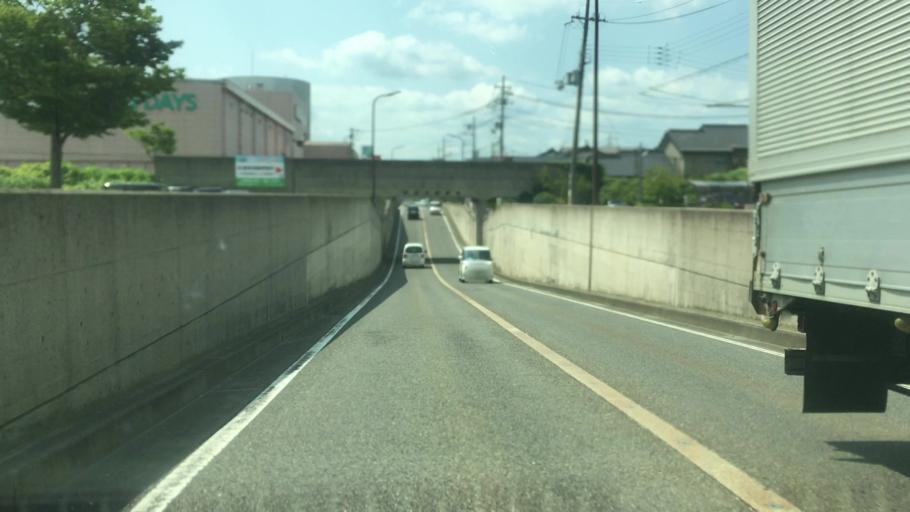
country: JP
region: Hyogo
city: Toyooka
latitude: 35.5520
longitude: 134.8155
